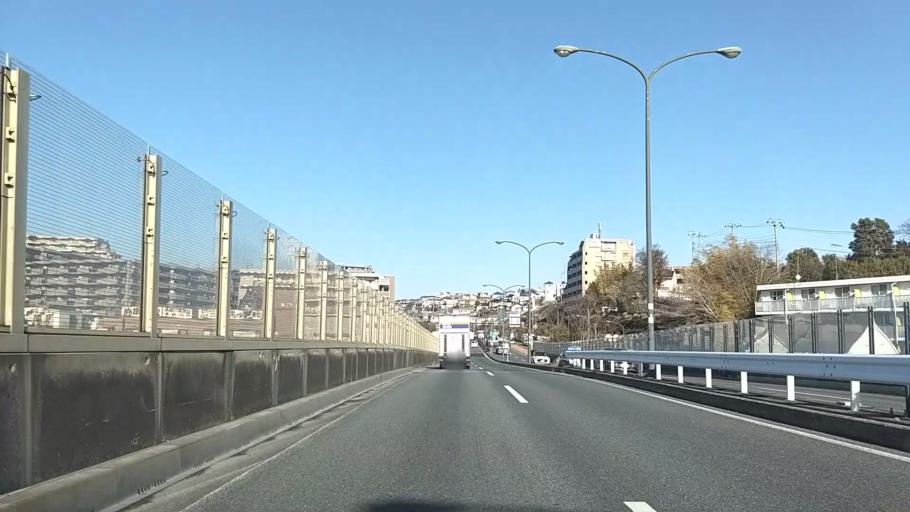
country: JP
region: Kanagawa
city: Yokohama
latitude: 35.3961
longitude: 139.5827
